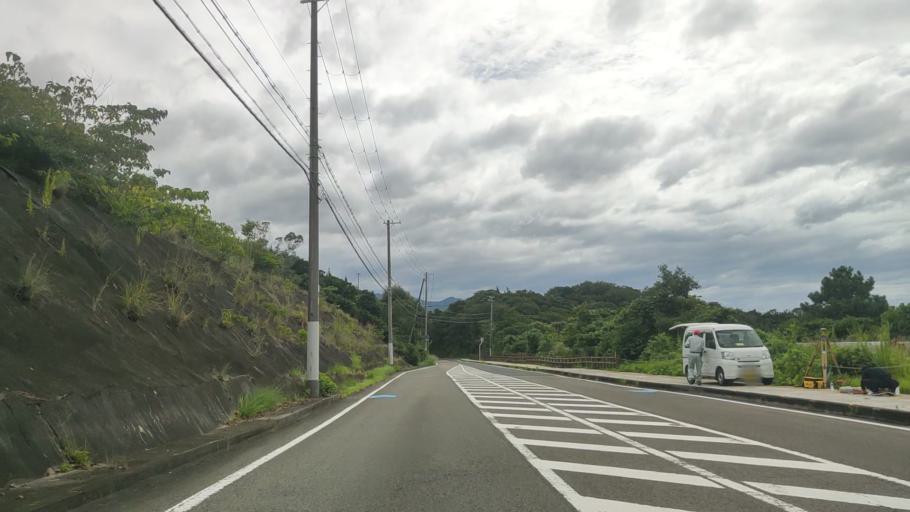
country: JP
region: Wakayama
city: Tanabe
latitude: 33.6627
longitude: 135.3740
